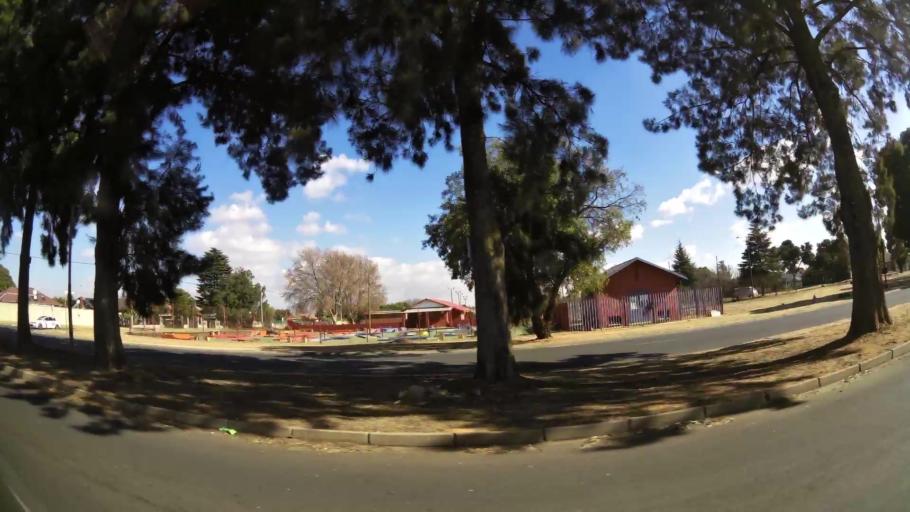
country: ZA
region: Gauteng
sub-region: City of Johannesburg Metropolitan Municipality
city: Roodepoort
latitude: -26.1366
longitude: 27.8337
